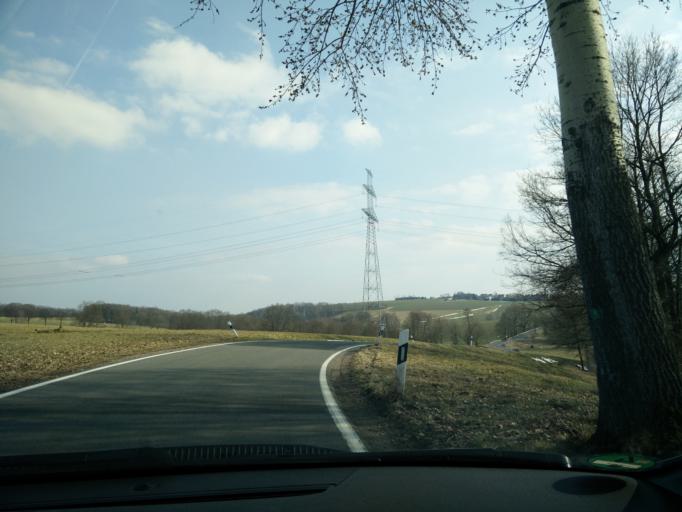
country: DE
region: Saxony
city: Colditz
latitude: 51.1139
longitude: 12.8152
